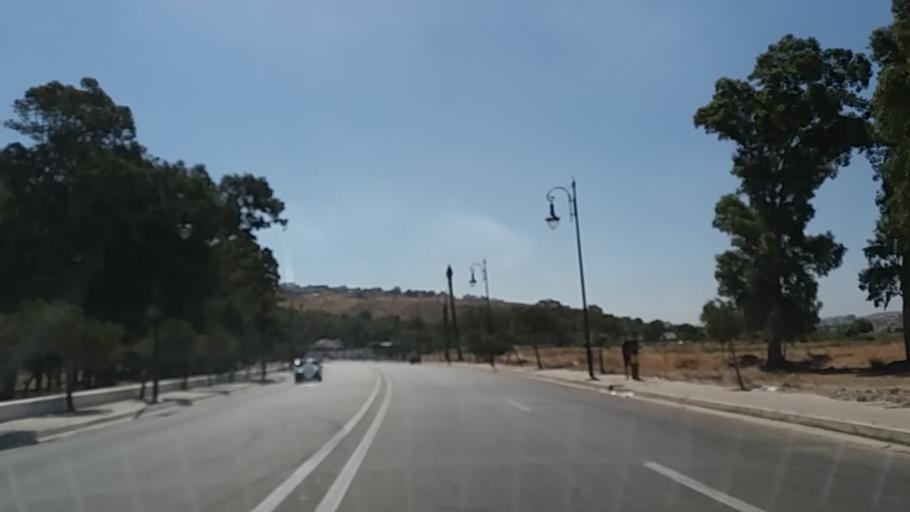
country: MA
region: Tanger-Tetouan
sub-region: Tanger-Assilah
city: Tangier
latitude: 35.7789
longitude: -5.7641
